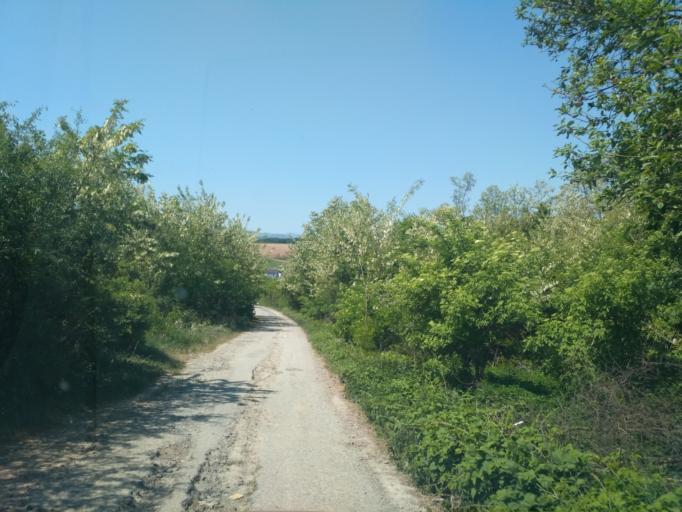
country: SK
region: Kosicky
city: Kosice
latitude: 48.7920
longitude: 21.3656
